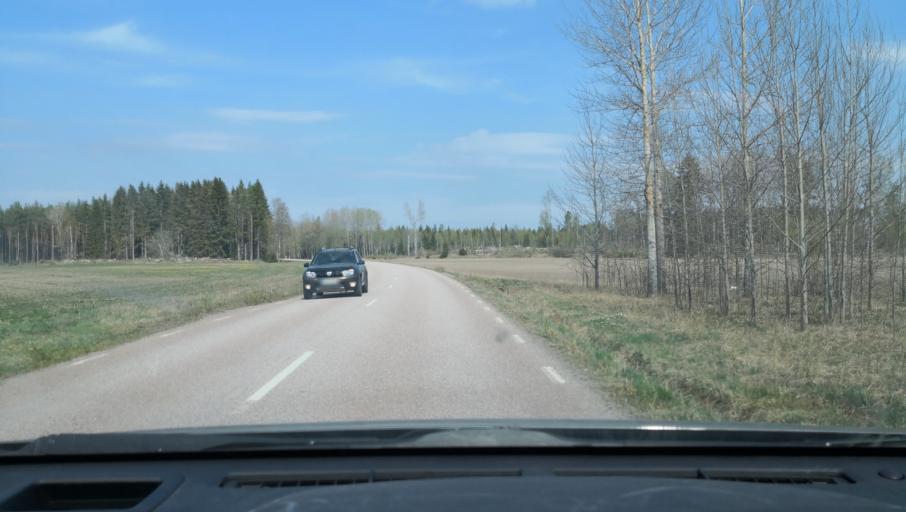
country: SE
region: Vaestmanland
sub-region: Vasteras
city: Skultuna
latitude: 59.7463
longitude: 16.4112
